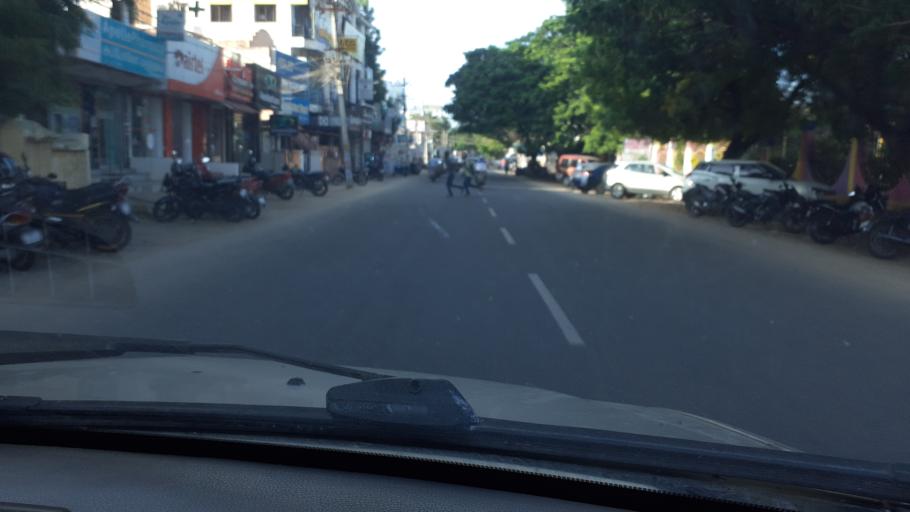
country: IN
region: Tamil Nadu
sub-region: Tirunelveli Kattabo
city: Tirunelveli
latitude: 8.7213
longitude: 77.7322
